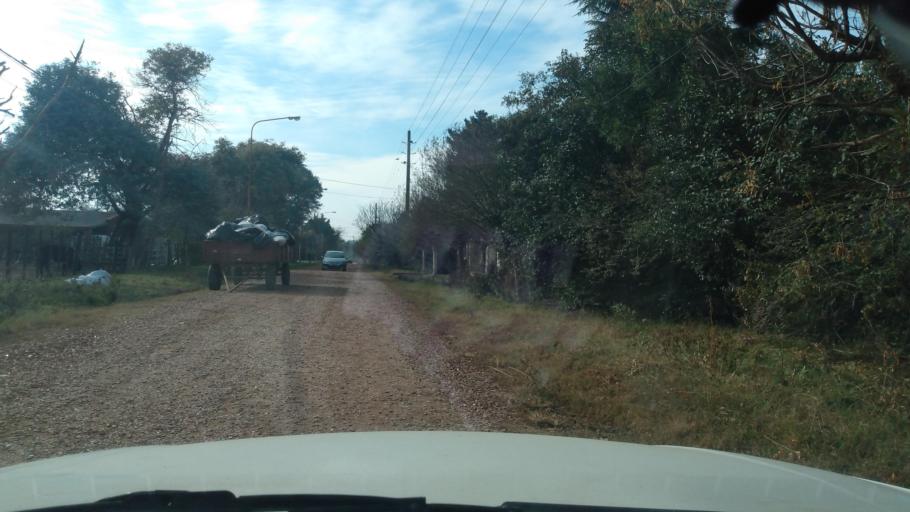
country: AR
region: Buenos Aires
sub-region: Partido de Lujan
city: Lujan
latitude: -34.5879
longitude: -59.1267
